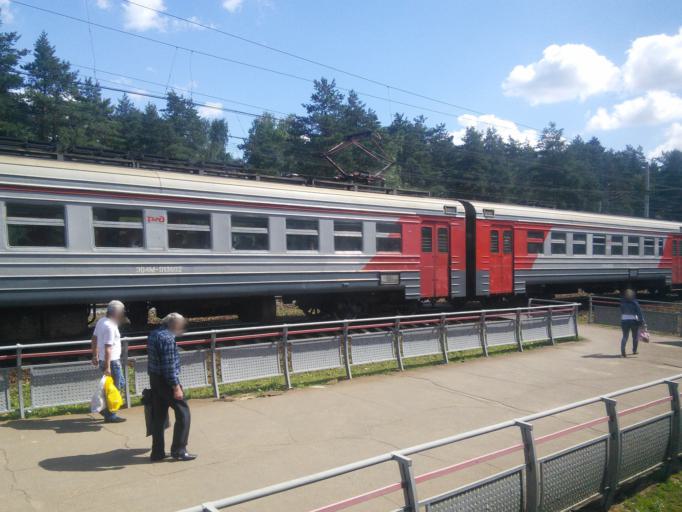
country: RU
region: Moskovskaya
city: Kratovo
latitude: 55.5816
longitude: 38.1851
